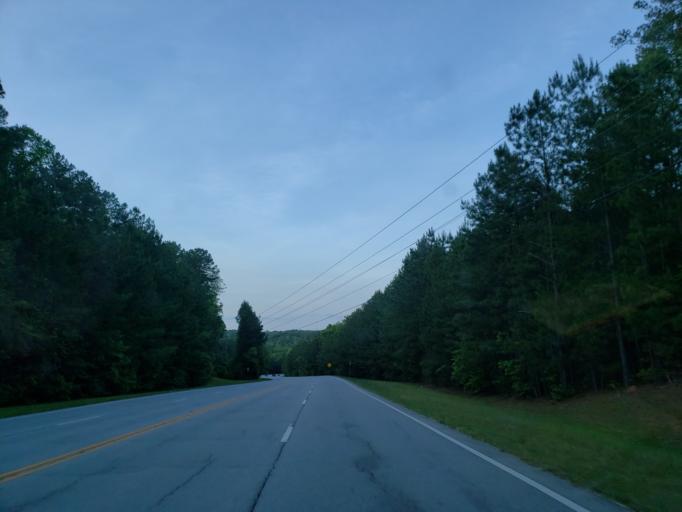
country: US
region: Georgia
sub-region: Fulton County
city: Chattahoochee Hills
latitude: 33.6489
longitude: -84.8235
